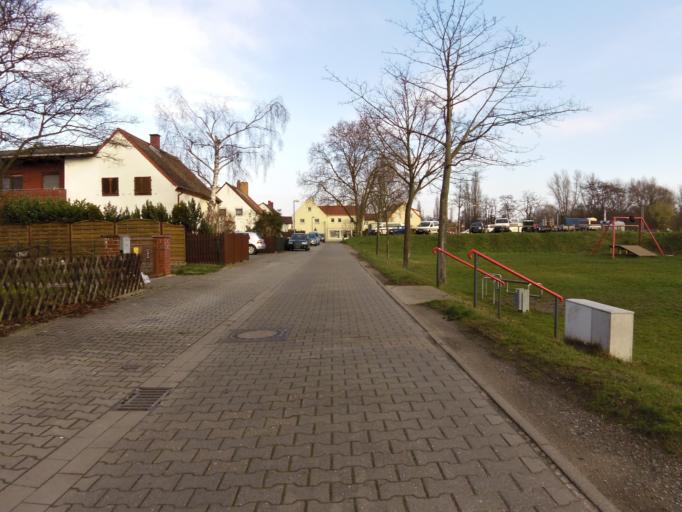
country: DE
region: Rheinland-Pfalz
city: Worms
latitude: 49.6102
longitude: 8.3575
